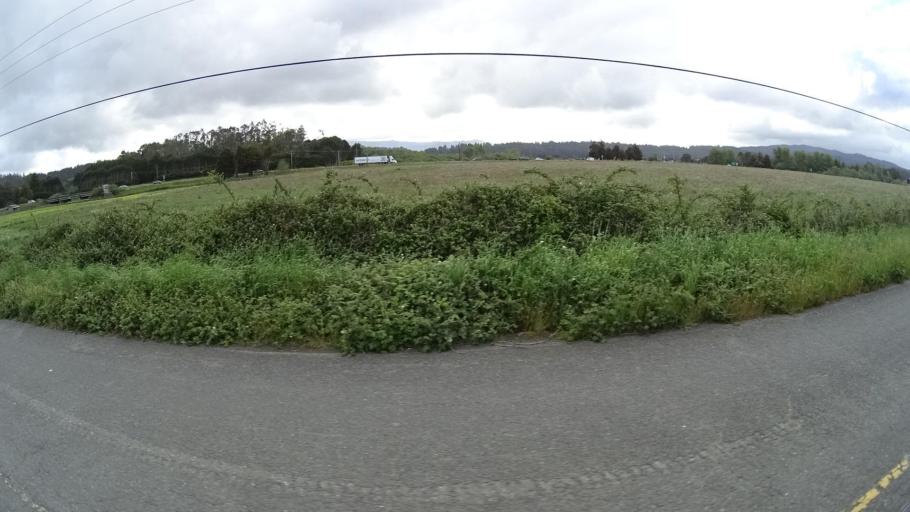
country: US
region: California
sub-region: Humboldt County
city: McKinleyville
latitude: 40.9081
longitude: -124.0914
